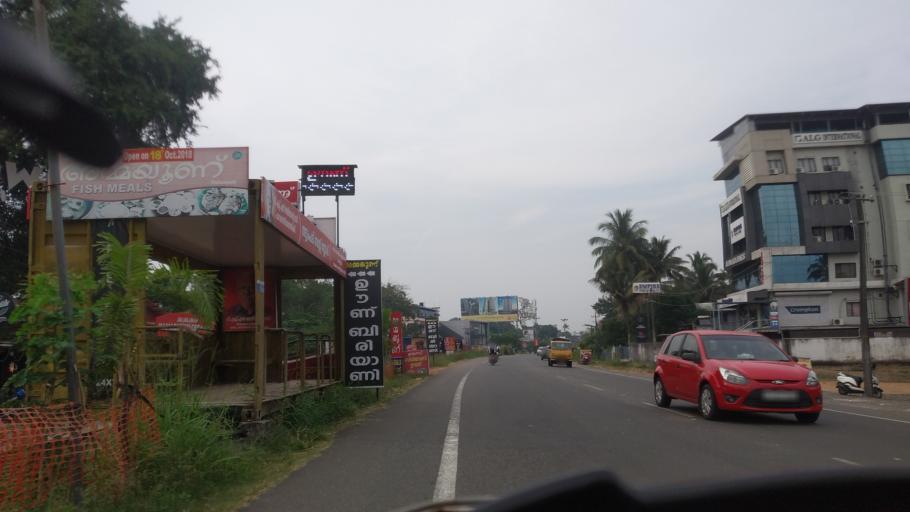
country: IN
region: Kerala
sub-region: Ernakulam
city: Elur
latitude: 10.0489
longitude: 76.2949
